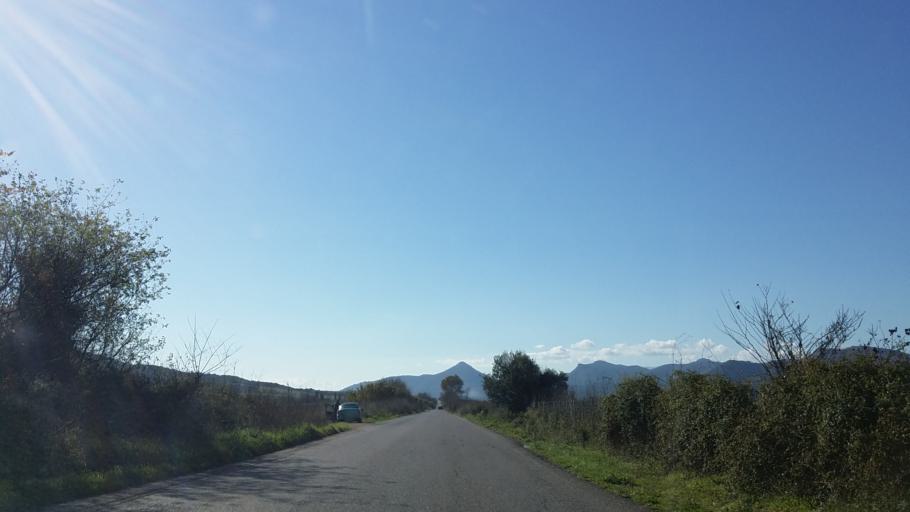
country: GR
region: West Greece
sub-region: Nomos Aitolias kai Akarnanias
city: Vonitsa
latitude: 38.8649
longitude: 20.8817
